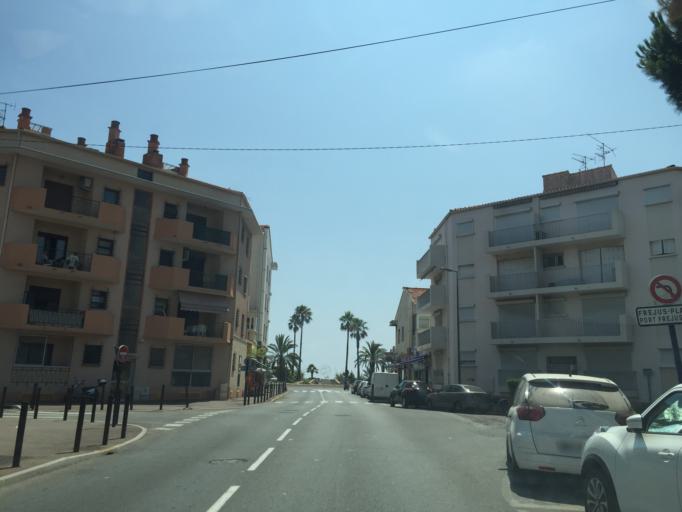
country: FR
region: Provence-Alpes-Cote d'Azur
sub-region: Departement du Var
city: Saint-Raphael
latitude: 43.4256
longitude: 6.7624
